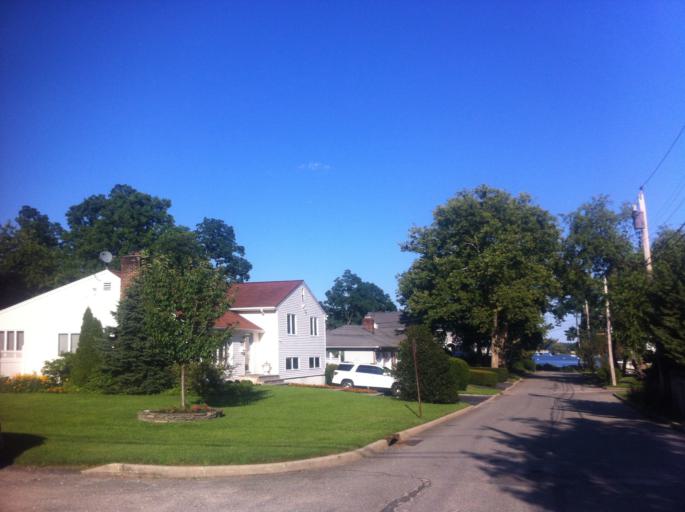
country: US
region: New York
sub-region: Nassau County
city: Bayville
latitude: 40.9054
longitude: -73.5598
